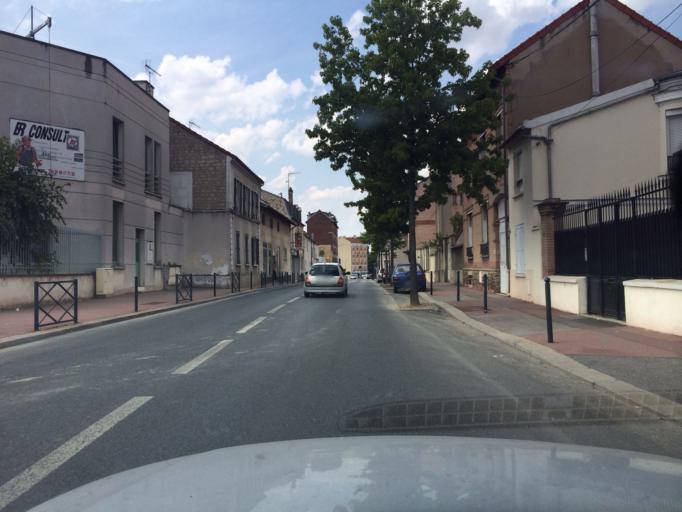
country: FR
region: Ile-de-France
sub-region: Departement du Val-de-Marne
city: Creteil
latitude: 48.7986
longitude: 2.4750
